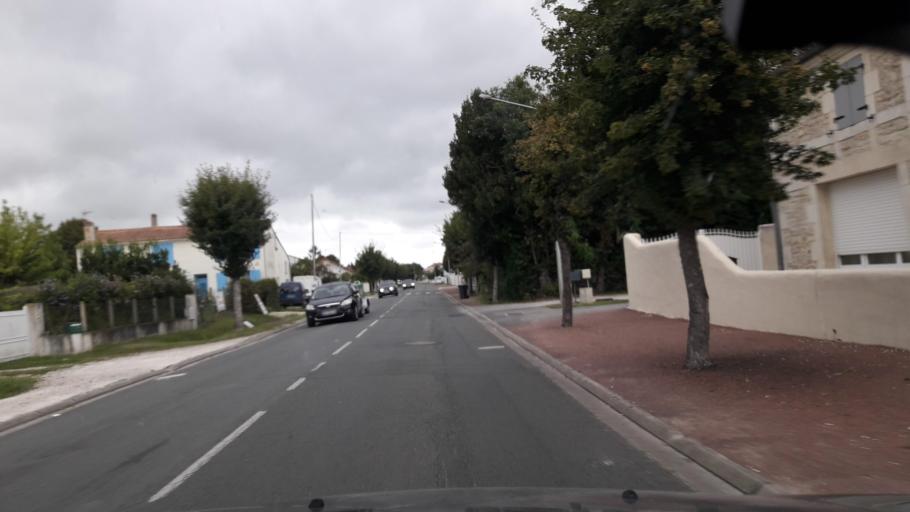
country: FR
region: Poitou-Charentes
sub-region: Departement de la Charente-Maritime
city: Etaules
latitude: 45.7383
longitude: -1.1104
